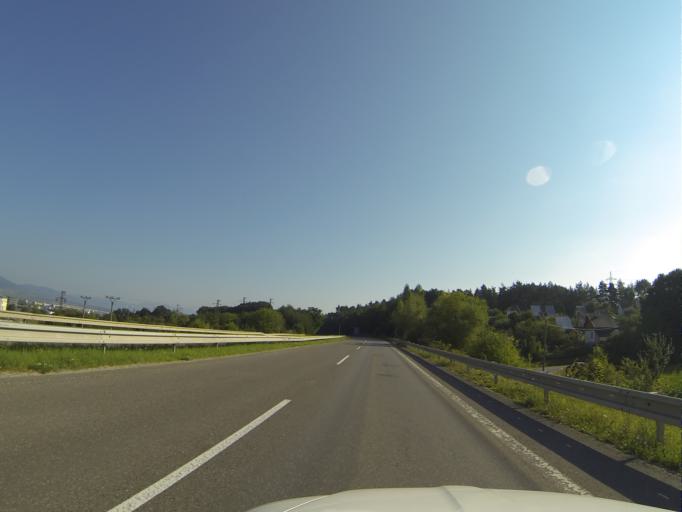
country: SK
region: Nitriansky
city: Prievidza
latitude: 48.7490
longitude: 18.6258
